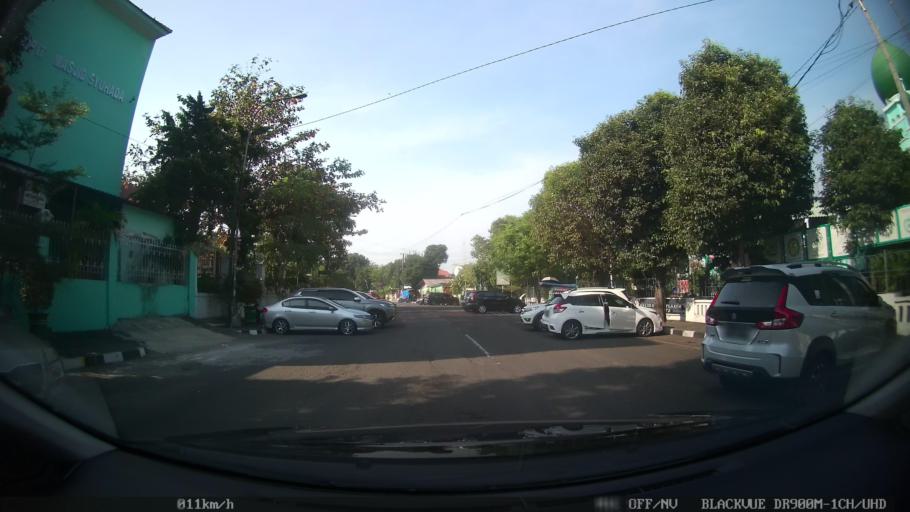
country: ID
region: Daerah Istimewa Yogyakarta
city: Yogyakarta
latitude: -7.7861
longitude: 110.3696
